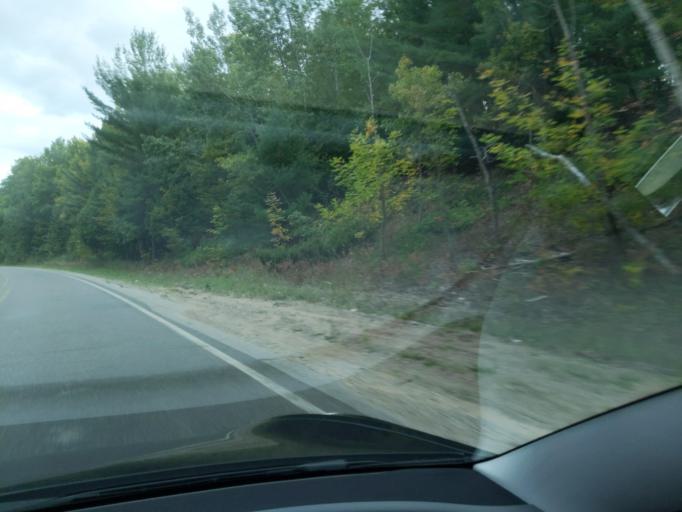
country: US
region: Michigan
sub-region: Kalkaska County
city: Rapid City
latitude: 44.7851
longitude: -85.2773
